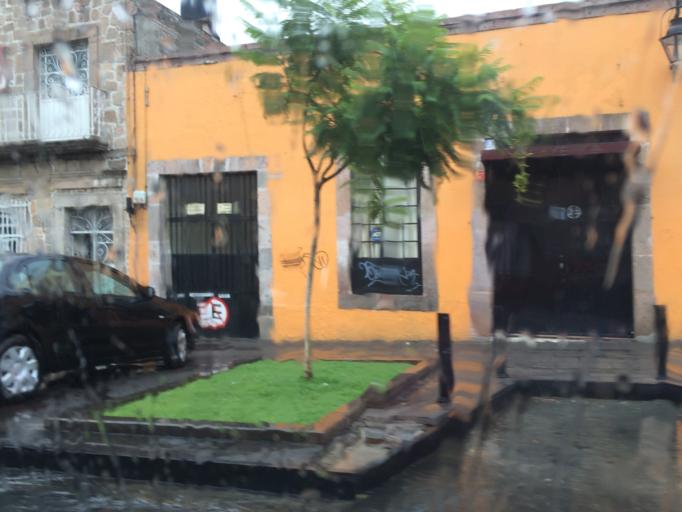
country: MX
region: Michoacan
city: Morelia
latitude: 19.7030
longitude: -101.2008
